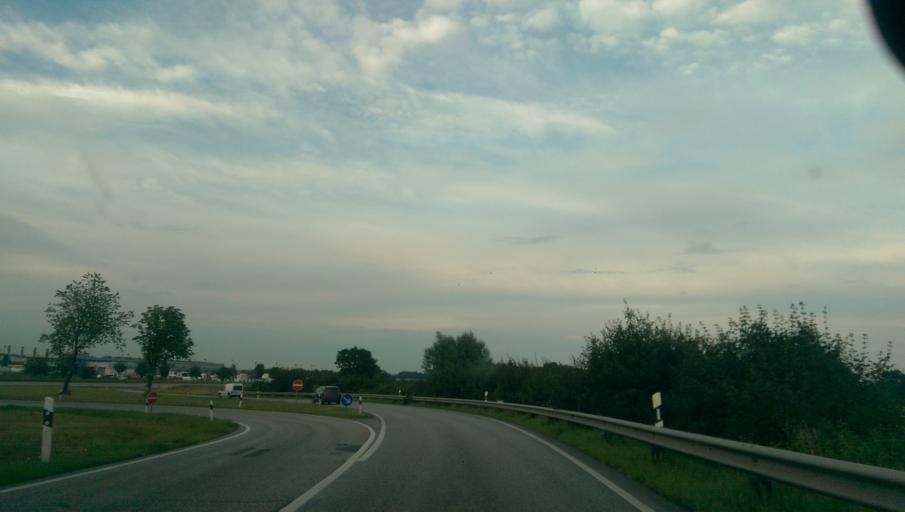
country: DE
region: Schleswig-Holstein
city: Barnitz
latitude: 53.8191
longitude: 10.5083
